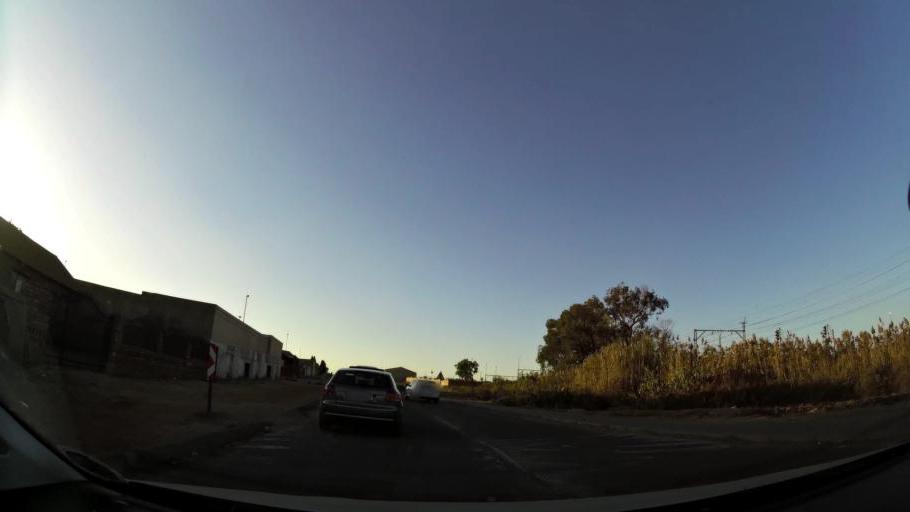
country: ZA
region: Gauteng
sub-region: Ekurhuleni Metropolitan Municipality
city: Tembisa
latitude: -26.0137
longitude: 28.2142
